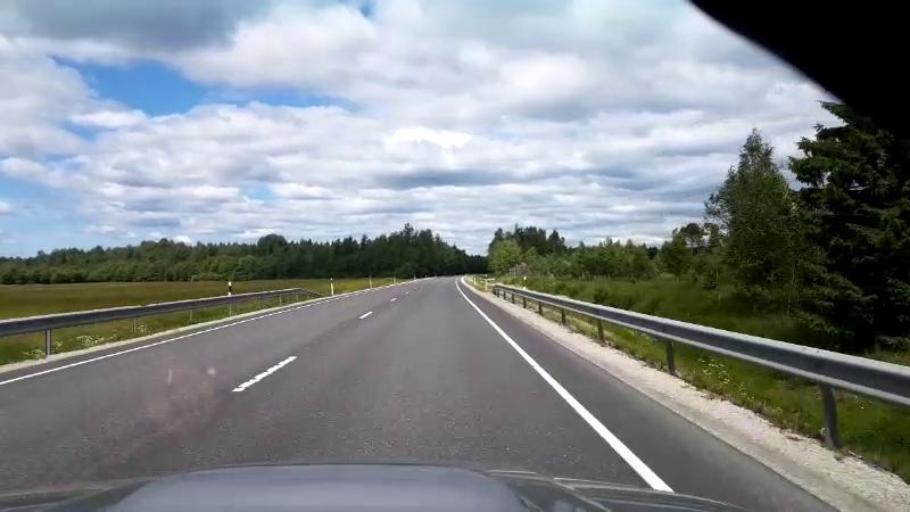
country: EE
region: Raplamaa
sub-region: Maerjamaa vald
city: Marjamaa
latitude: 58.8213
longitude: 24.4134
